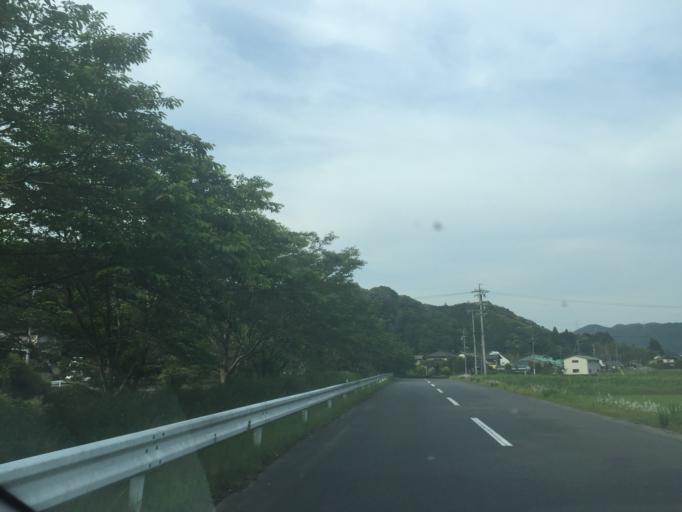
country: JP
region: Shizuoka
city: Mori
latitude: 34.8428
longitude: 137.9821
